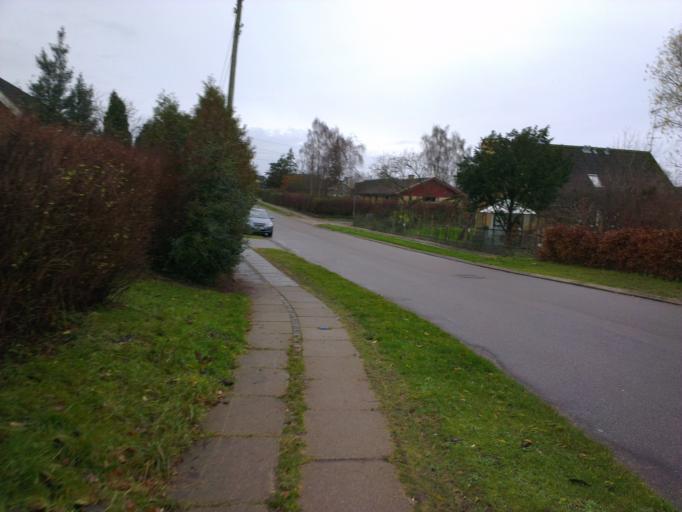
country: DK
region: Capital Region
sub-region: Frederikssund Kommune
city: Jaegerspris
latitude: 55.8545
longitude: 12.0013
